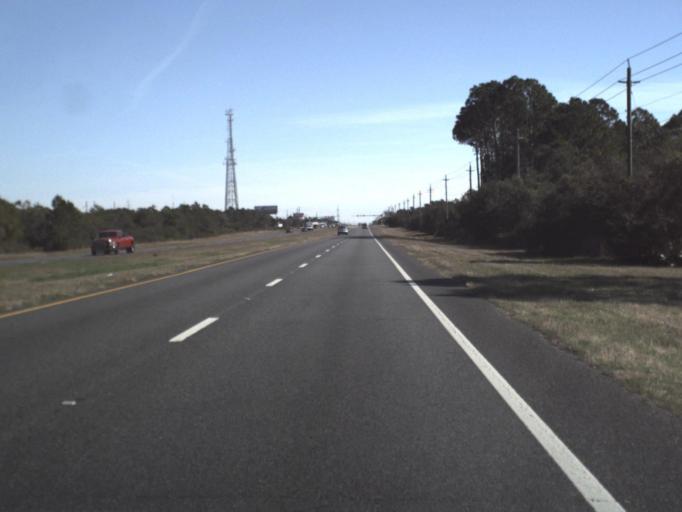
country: US
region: Florida
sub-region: Bay County
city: Laguna Beach
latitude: 30.2573
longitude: -85.9471
